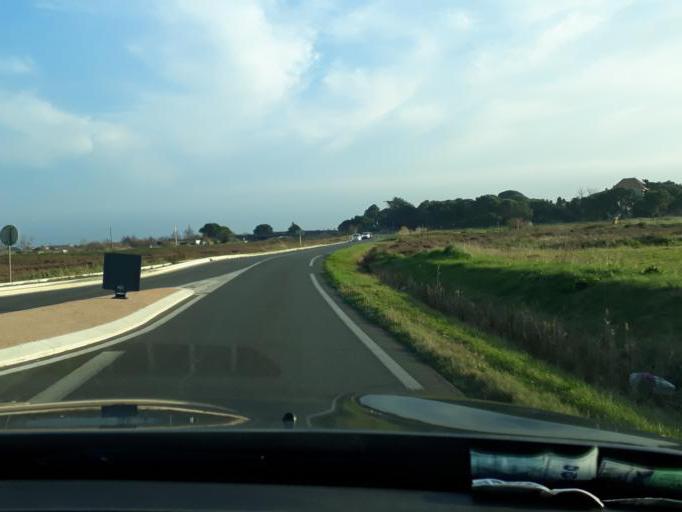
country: FR
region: Languedoc-Roussillon
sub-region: Departement de l'Herault
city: Marseillan
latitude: 43.3244
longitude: 3.5310
